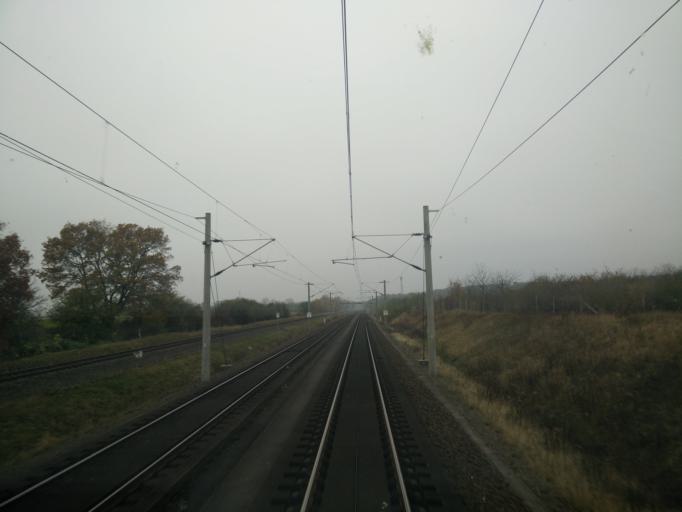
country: DE
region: Brandenburg
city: Pawesin
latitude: 52.5813
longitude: 12.7760
